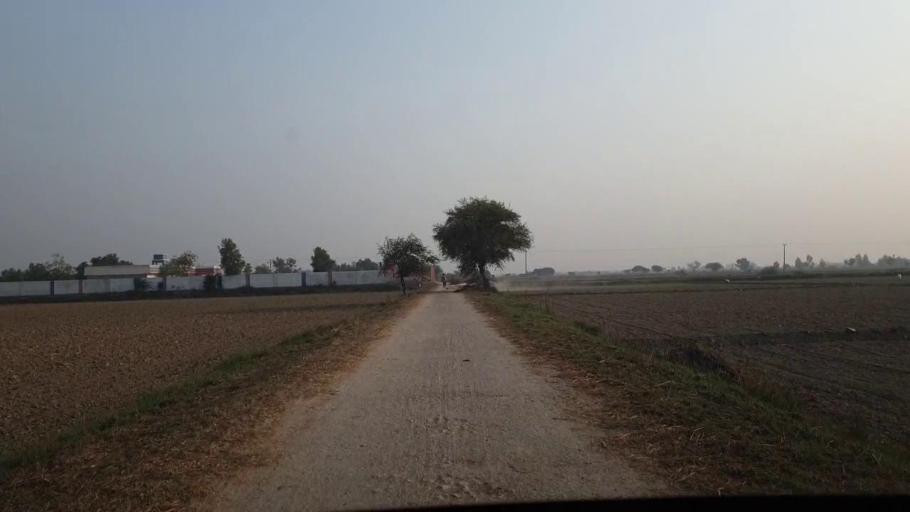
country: PK
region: Sindh
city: Chuhar Jamali
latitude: 24.2572
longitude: 68.1127
